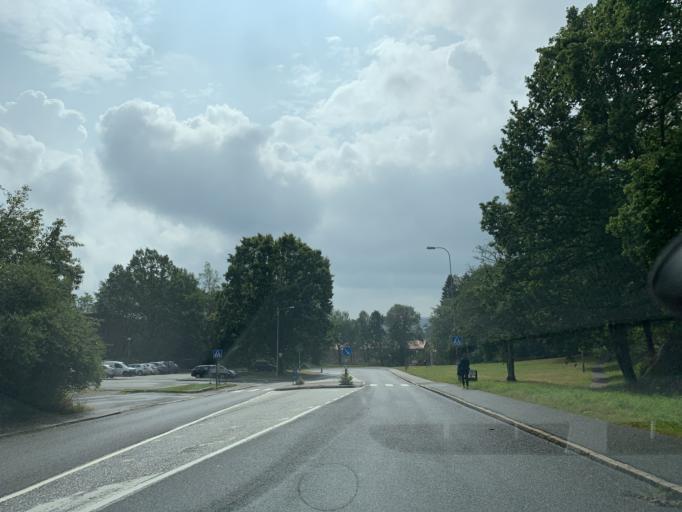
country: SE
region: Vaestra Goetaland
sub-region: Goteborg
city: Eriksbo
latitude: 57.7489
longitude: 12.0271
